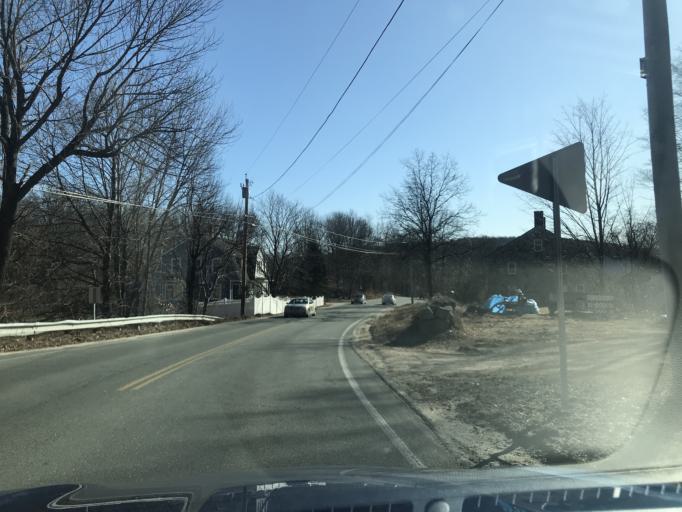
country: US
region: Massachusetts
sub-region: Essex County
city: North Andover
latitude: 42.7131
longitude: -71.0825
